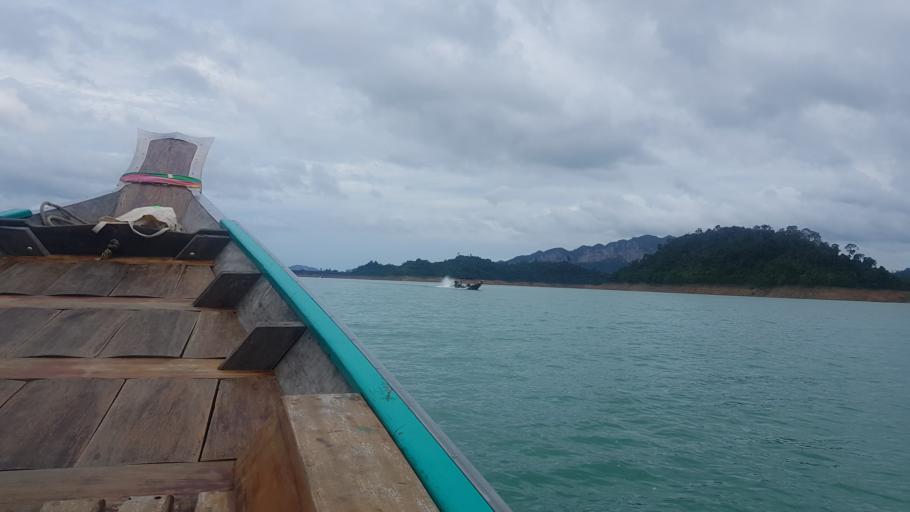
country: TH
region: Surat Thani
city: Ban Takhun
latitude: 8.9912
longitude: 98.7819
